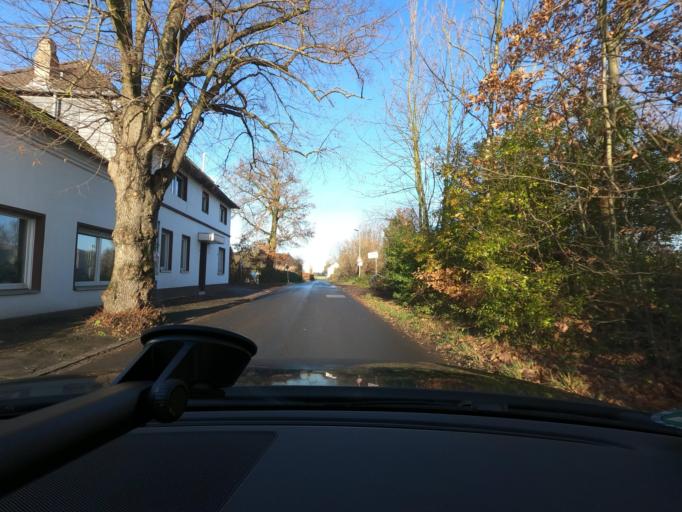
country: DE
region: North Rhine-Westphalia
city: Tonisvorst
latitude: 51.3459
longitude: 6.5191
